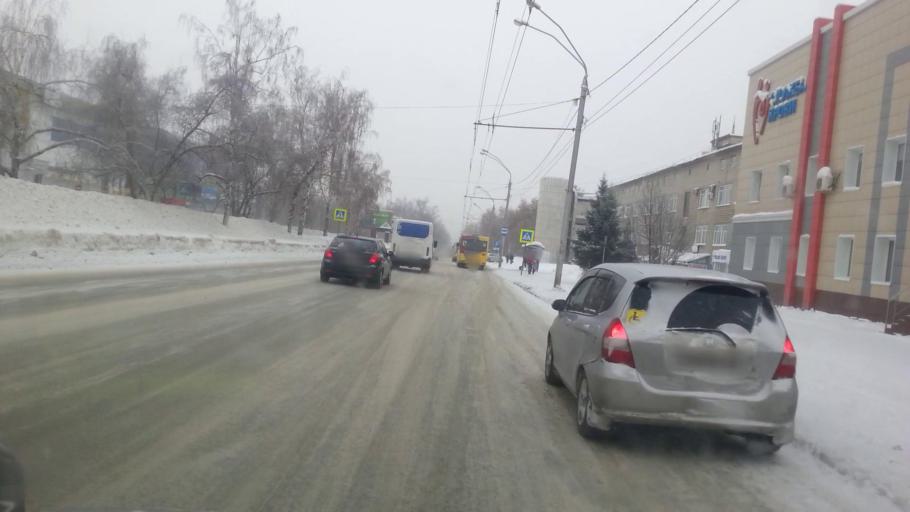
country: RU
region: Altai Krai
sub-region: Gorod Barnaulskiy
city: Barnaul
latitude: 53.3826
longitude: 83.7389
